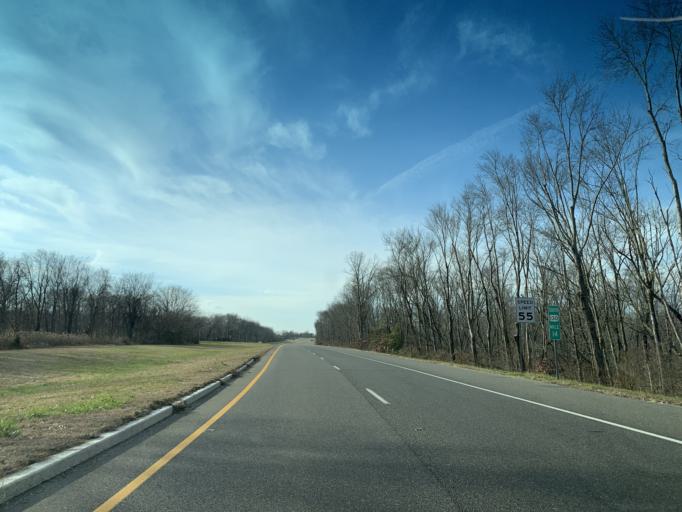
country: US
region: New Jersey
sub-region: Gloucester County
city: Gibbstown
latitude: 39.8042
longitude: -75.3131
